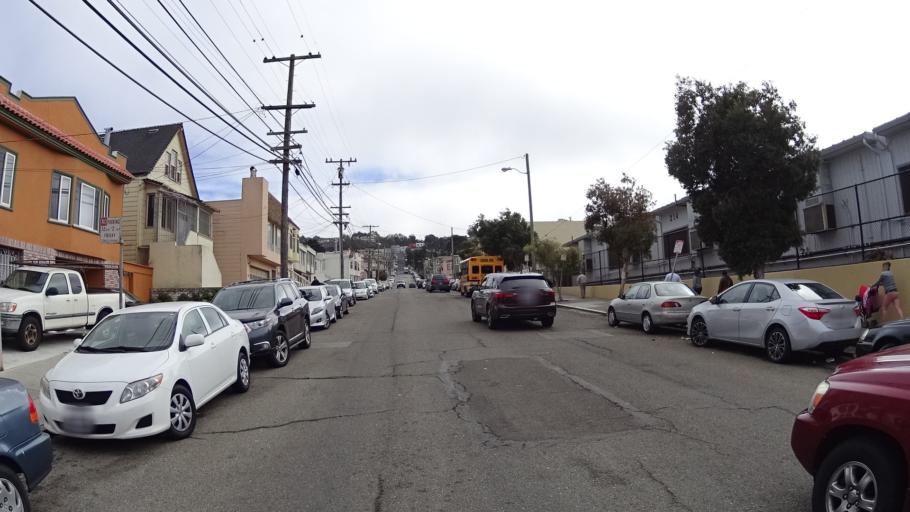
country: US
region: California
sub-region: San Mateo County
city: Daly City
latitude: 37.7109
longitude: -122.4461
